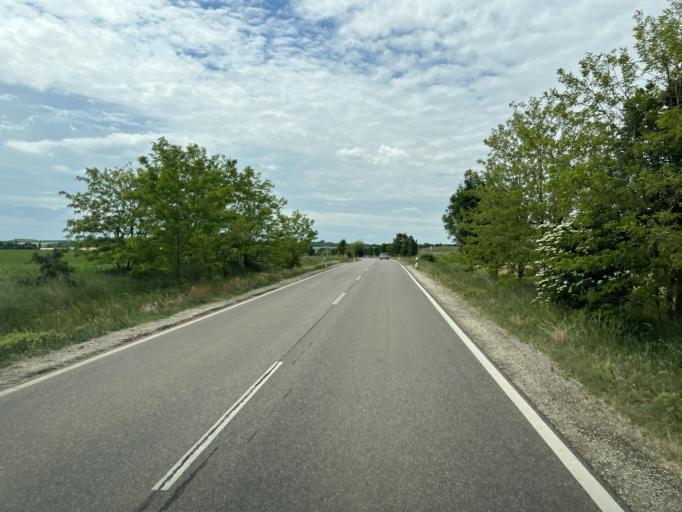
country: HU
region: Pest
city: Koka
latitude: 47.5103
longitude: 19.5963
